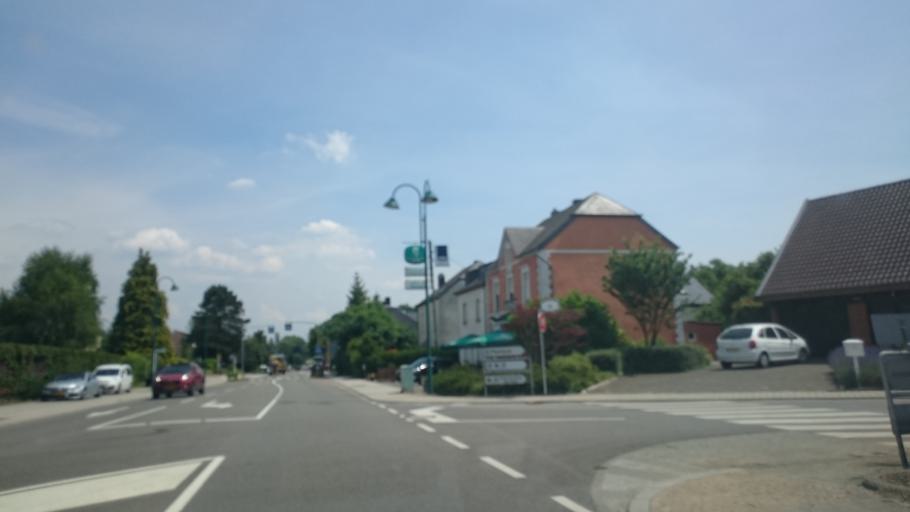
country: LU
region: Luxembourg
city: Capellen
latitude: 49.6440
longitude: 5.9932
